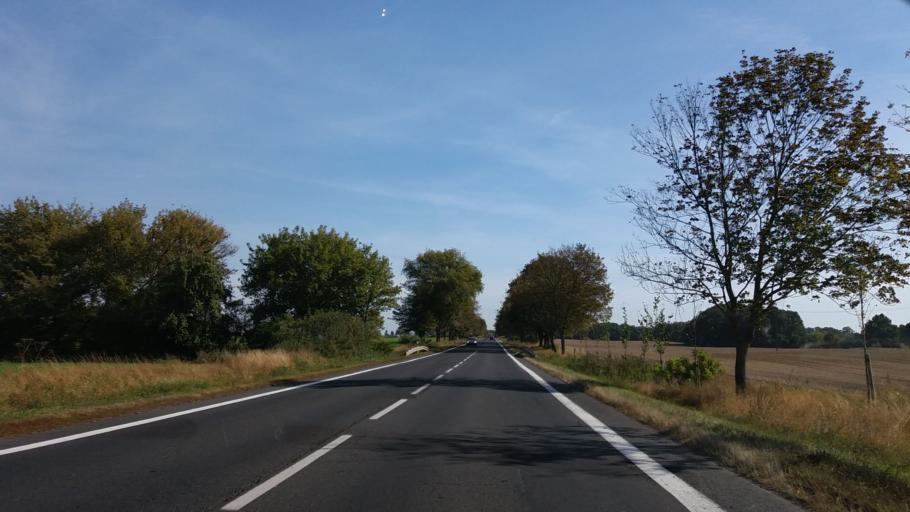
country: PL
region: Greater Poland Voivodeship
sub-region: Powiat miedzychodzki
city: Kwilcz
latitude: 52.5472
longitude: 16.1135
